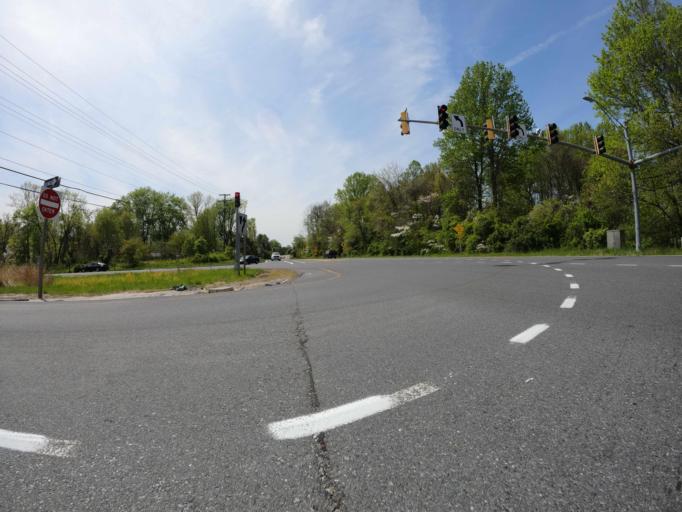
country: US
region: Maryland
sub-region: Howard County
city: Ellicott City
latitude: 39.3031
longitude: -76.8243
